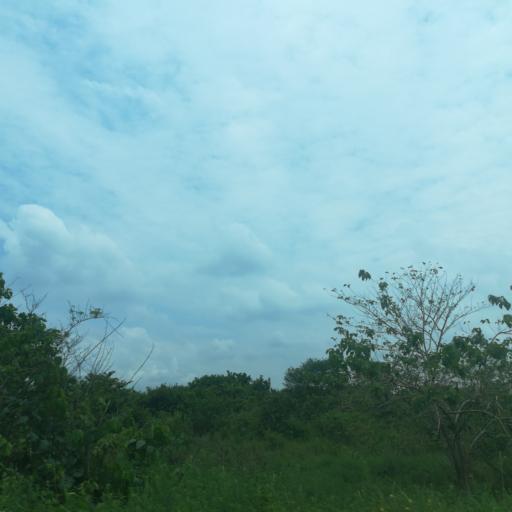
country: NG
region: Lagos
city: Ejirin
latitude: 6.6580
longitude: 3.8190
